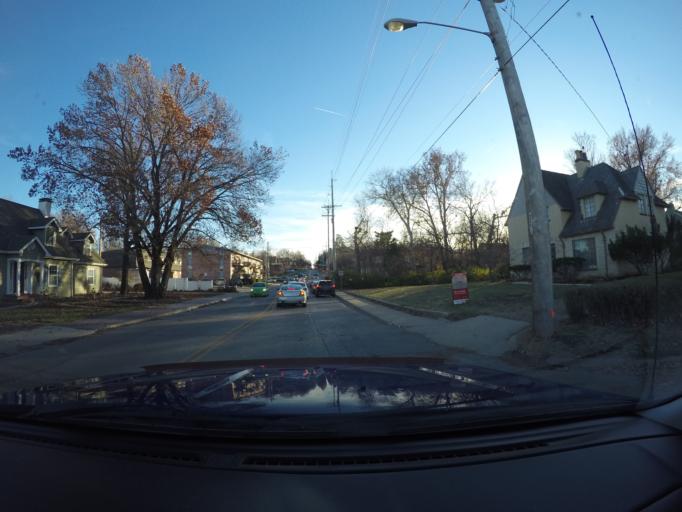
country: US
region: Kansas
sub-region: Riley County
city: Manhattan
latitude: 39.1870
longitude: -96.5888
